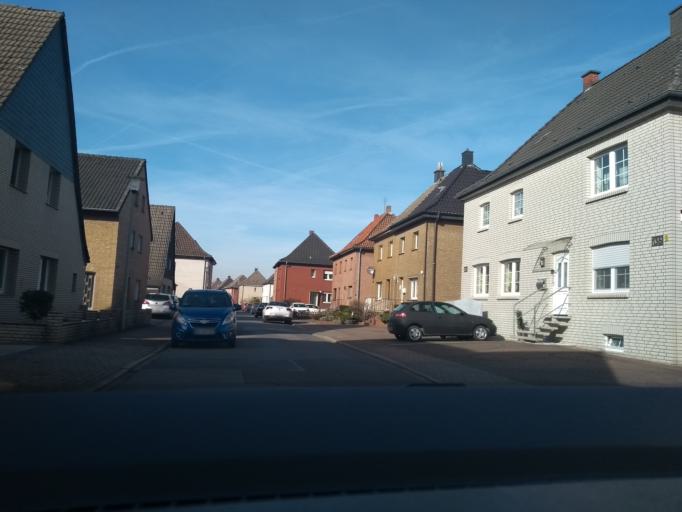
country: DE
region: North Rhine-Westphalia
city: Selm
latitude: 51.6963
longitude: 7.4594
